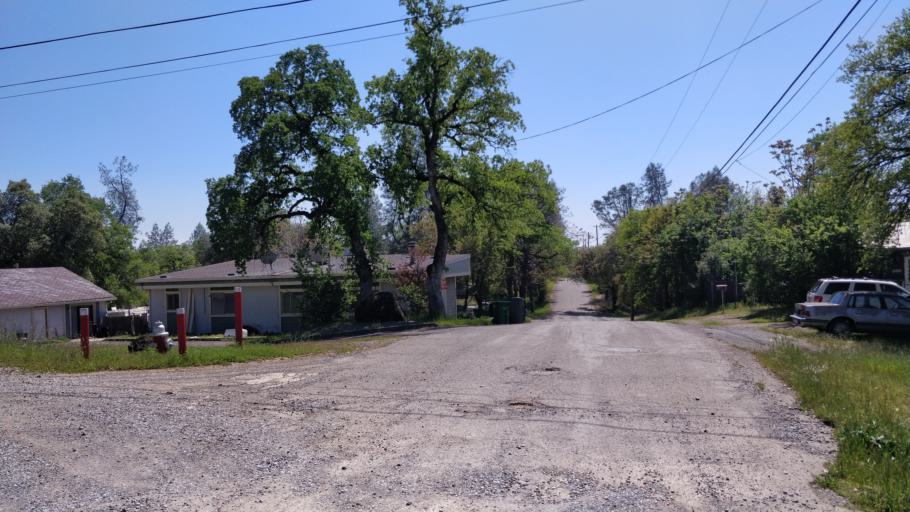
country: US
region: California
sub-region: Shasta County
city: Shasta Lake
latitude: 40.6682
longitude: -122.3559
